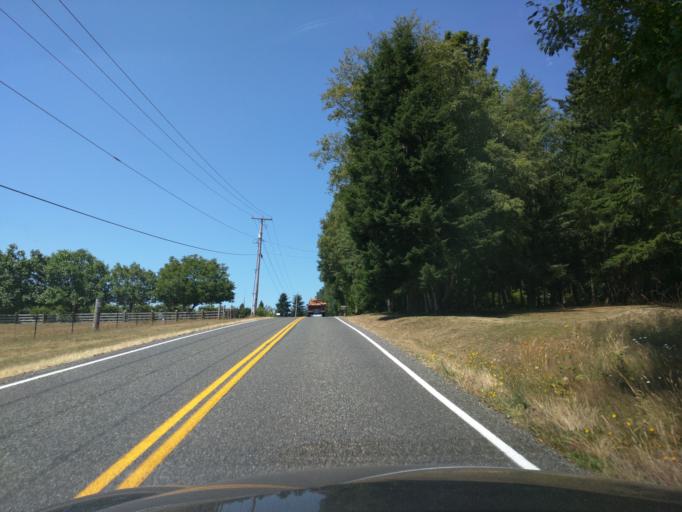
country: US
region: Washington
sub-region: Whatcom County
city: Blaine
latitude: 48.9935
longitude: -122.6548
